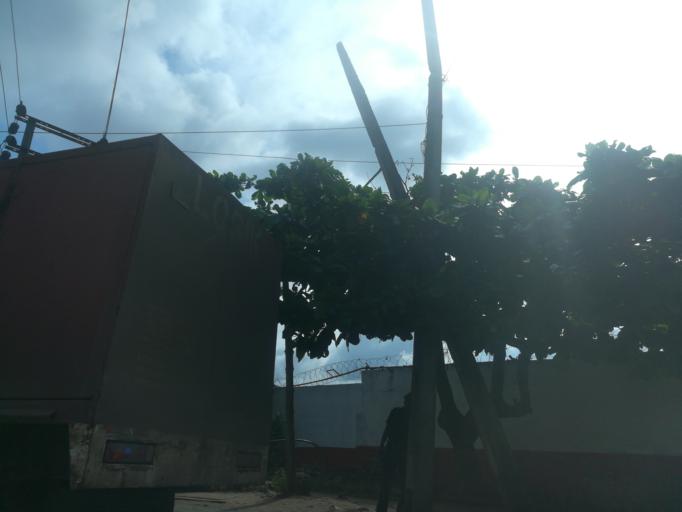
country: NG
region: Lagos
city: Ikeja
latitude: 6.6140
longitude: 3.3550
